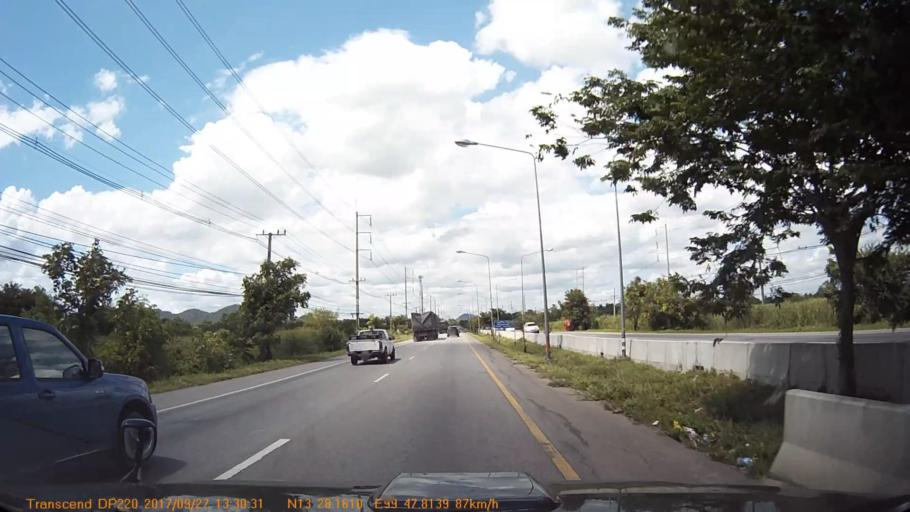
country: TH
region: Ratchaburi
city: Ratchaburi
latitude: 13.4692
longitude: 99.7969
